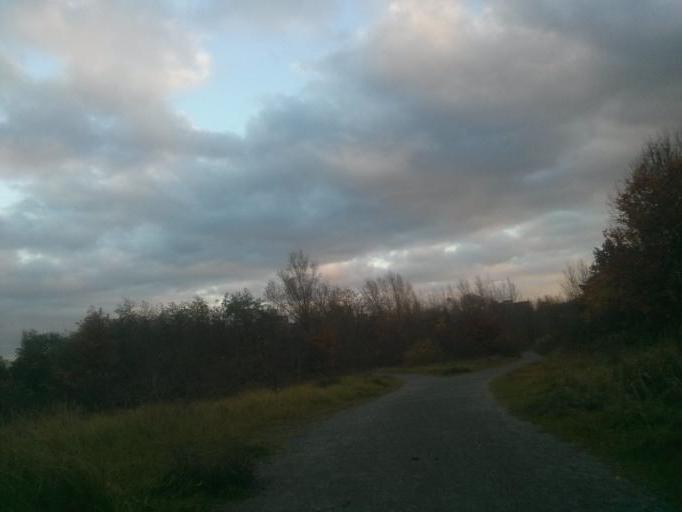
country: DE
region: North Rhine-Westphalia
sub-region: Regierungsbezirk Koln
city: Poll
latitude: 50.9032
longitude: 7.0111
